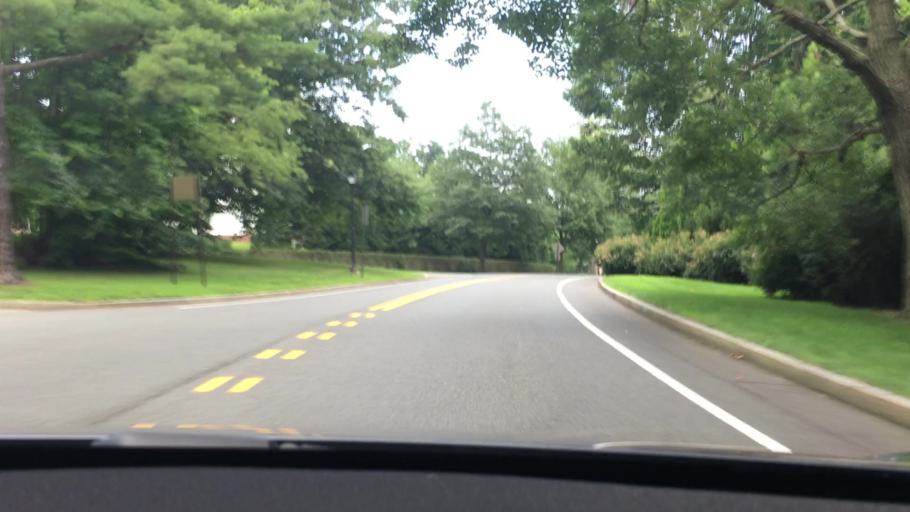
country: US
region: New York
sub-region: Westchester County
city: New Rochelle
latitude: 40.9312
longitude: -73.7832
